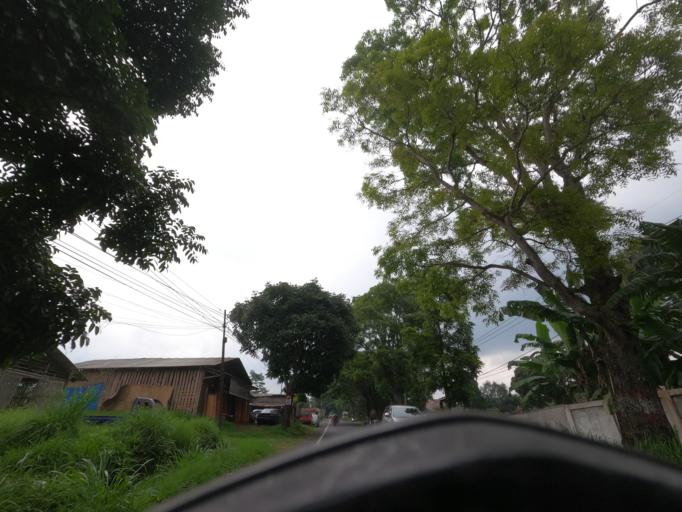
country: ID
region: West Java
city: Sukabumi
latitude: -6.7723
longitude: 107.0629
